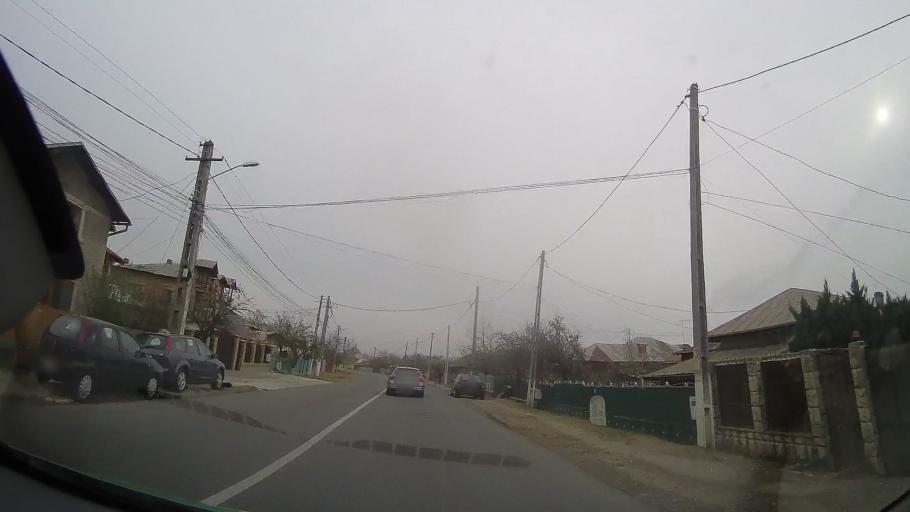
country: RO
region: Prahova
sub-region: Oras Baicoi
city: Tintea
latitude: 45.0313
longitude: 25.9056
